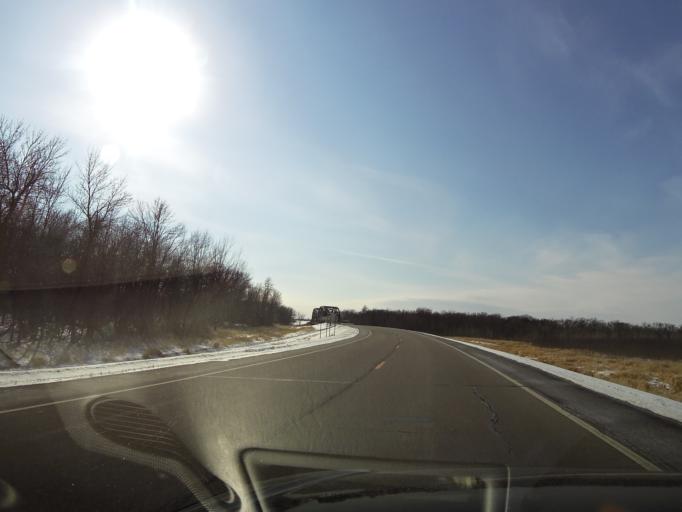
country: US
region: North Dakota
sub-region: Walsh County
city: Grafton
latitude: 48.4146
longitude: -97.1336
